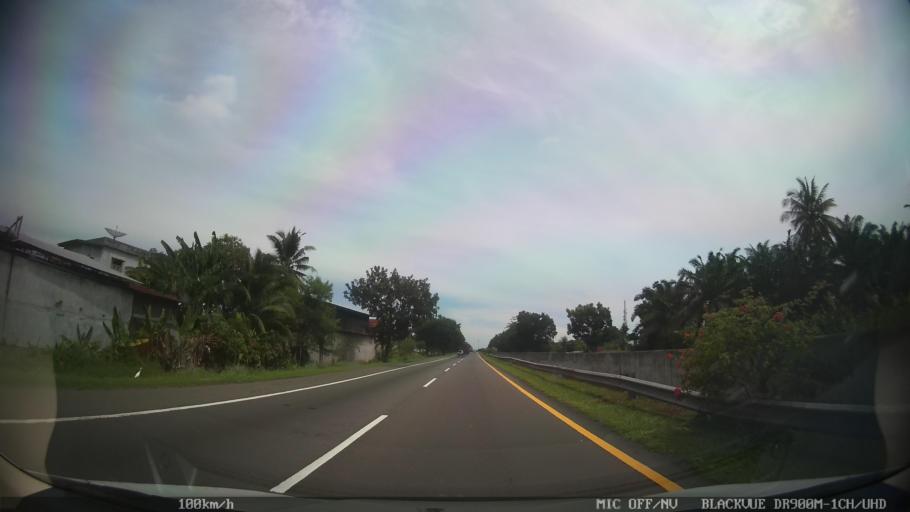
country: ID
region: North Sumatra
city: Labuhan Deli
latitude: 3.7029
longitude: 98.6816
